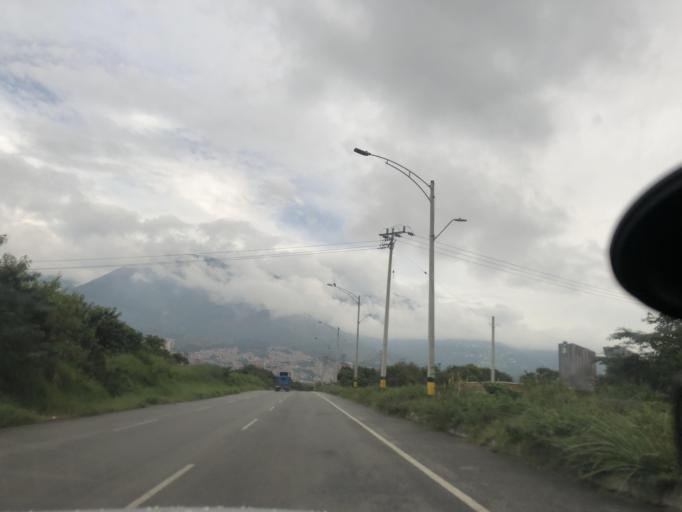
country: CO
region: Antioquia
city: Bello
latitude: 6.3216
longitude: -75.5542
